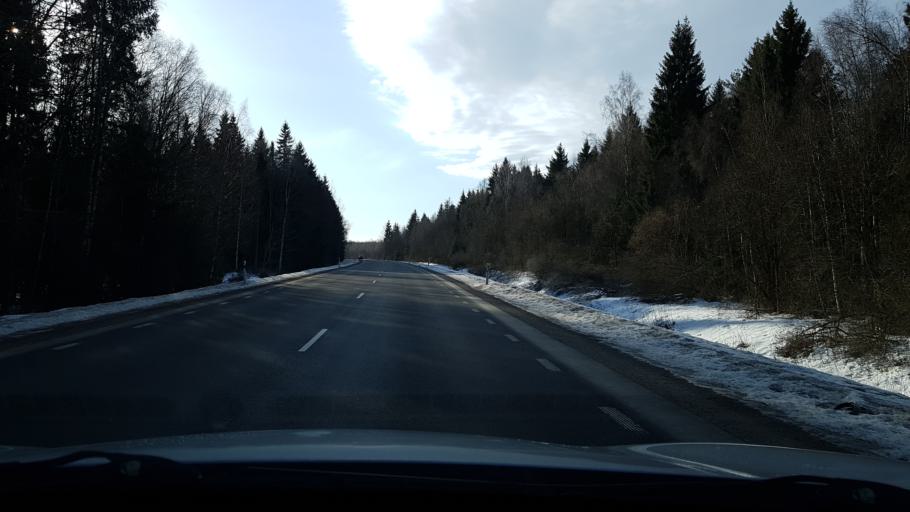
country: EE
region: Viljandimaa
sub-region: Vohma linn
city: Vohma
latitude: 58.5759
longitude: 25.5694
